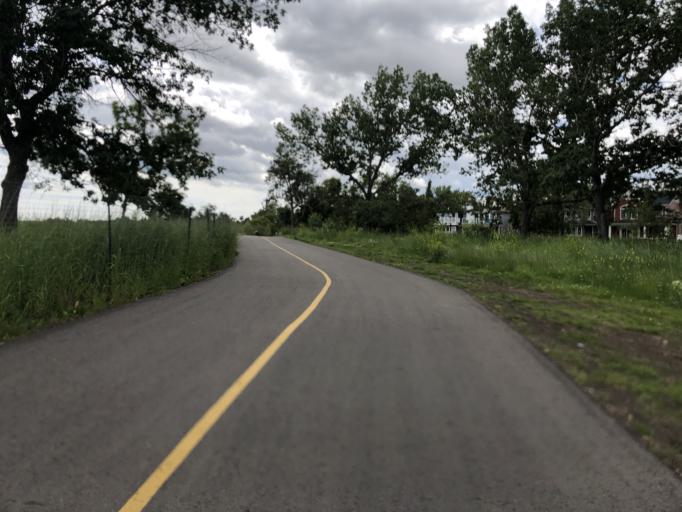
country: CA
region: Alberta
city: Calgary
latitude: 51.0362
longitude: -114.0144
